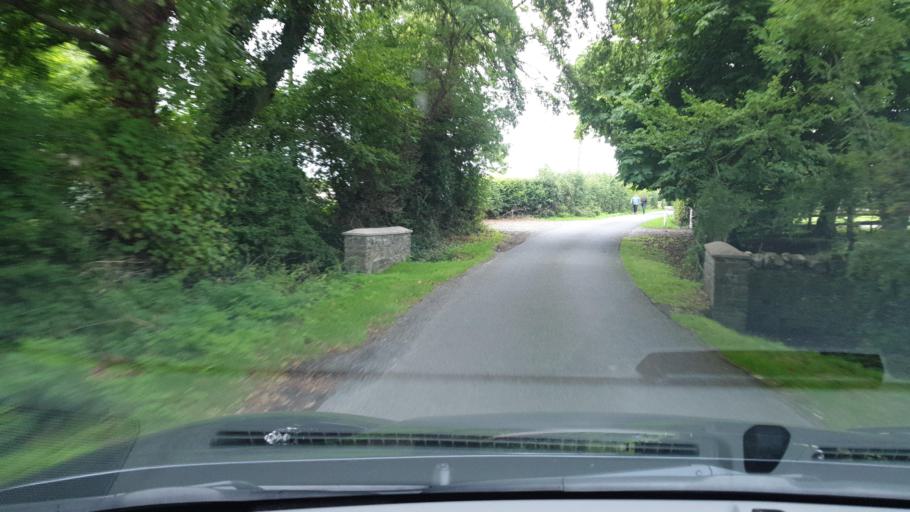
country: IE
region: Leinster
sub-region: An Mhi
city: Dunshaughlin
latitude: 53.4932
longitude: -6.5470
